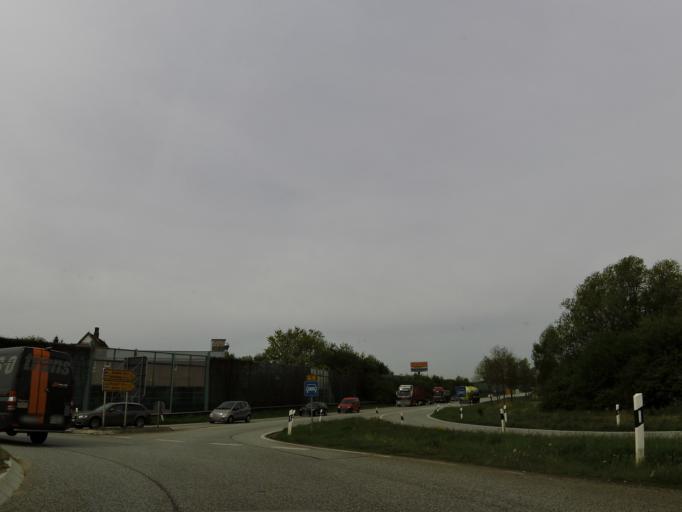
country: DE
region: Schleswig-Holstein
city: Heiligenstedten
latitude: 53.9340
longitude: 9.4789
